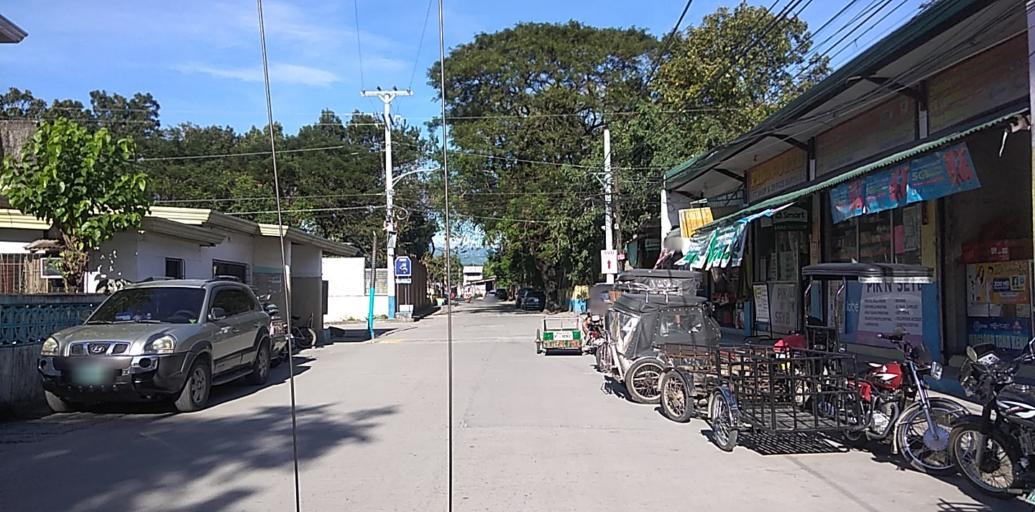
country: PH
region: Central Luzon
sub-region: Province of Pampanga
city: Porac
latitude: 15.0734
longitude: 120.5403
